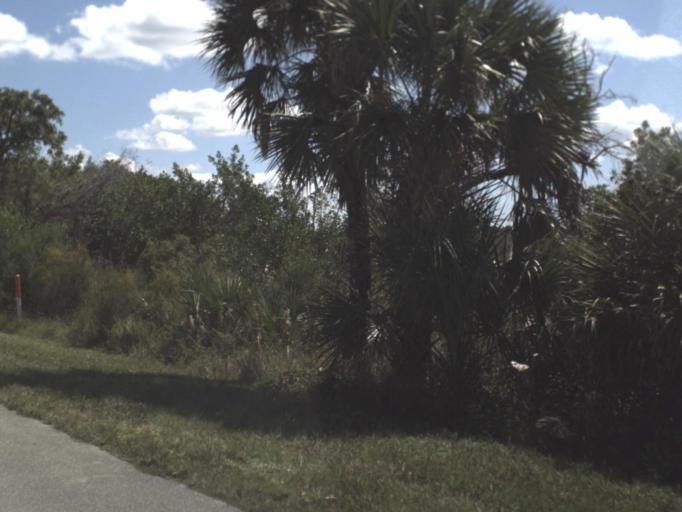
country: US
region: Florida
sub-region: Collier County
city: Marco
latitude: 25.9700
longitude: -81.5421
